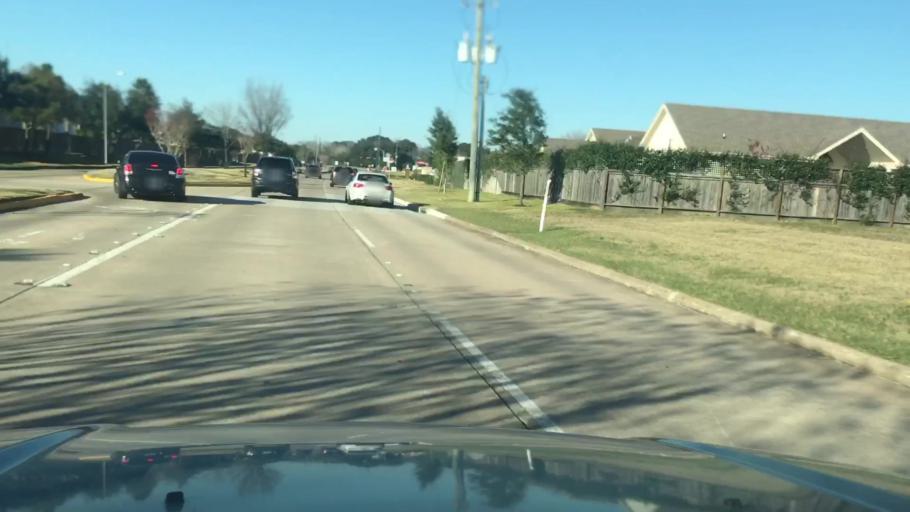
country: US
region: Texas
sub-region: Harris County
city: Katy
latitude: 29.8250
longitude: -95.7537
